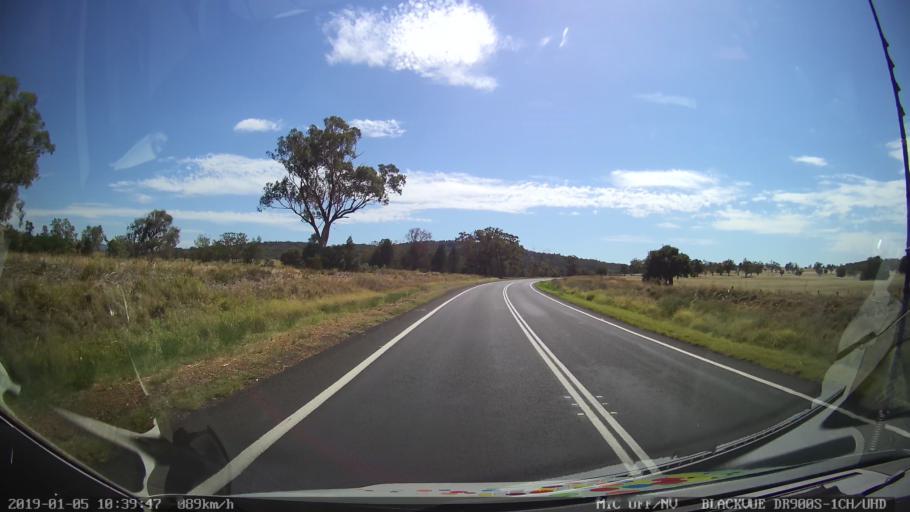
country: AU
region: New South Wales
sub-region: Gilgandra
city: Gilgandra
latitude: -31.4666
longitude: 148.9349
